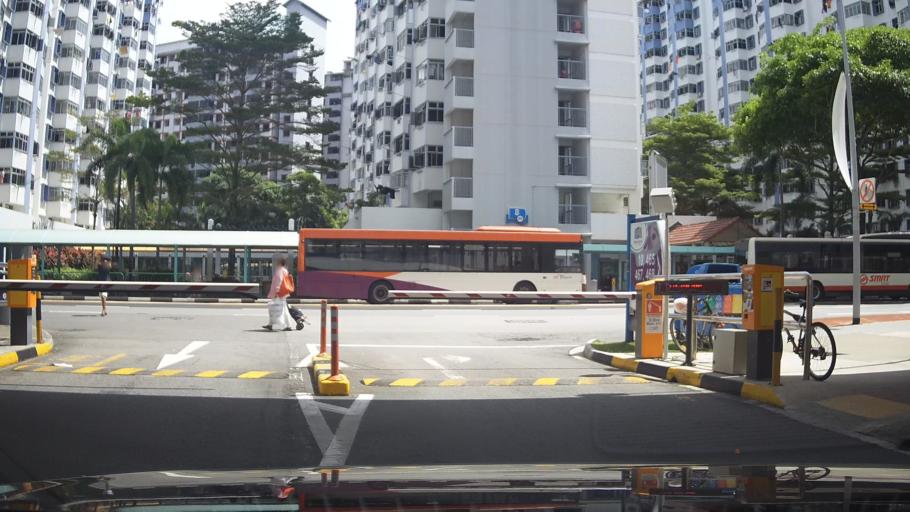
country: SG
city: Singapore
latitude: 1.3056
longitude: 103.8633
